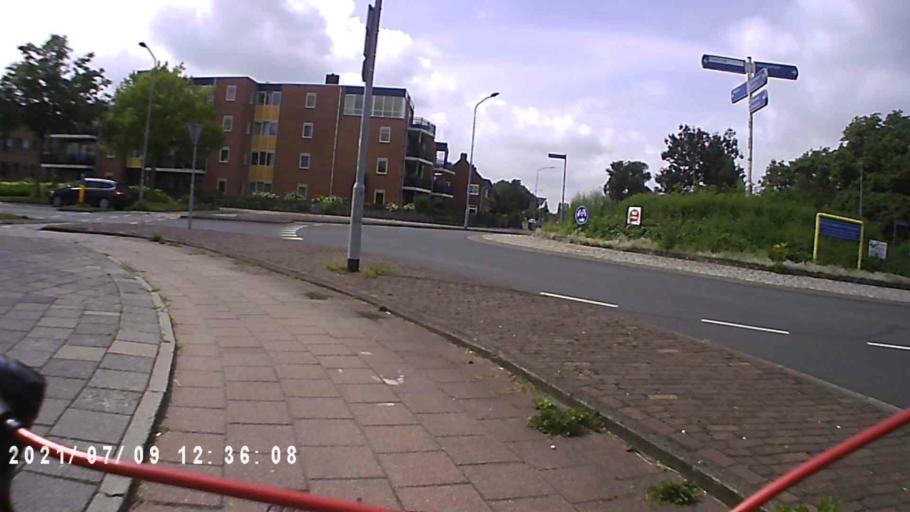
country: NL
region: Groningen
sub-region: Gemeente  Oldambt
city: Winschoten
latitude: 53.1482
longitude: 7.0252
